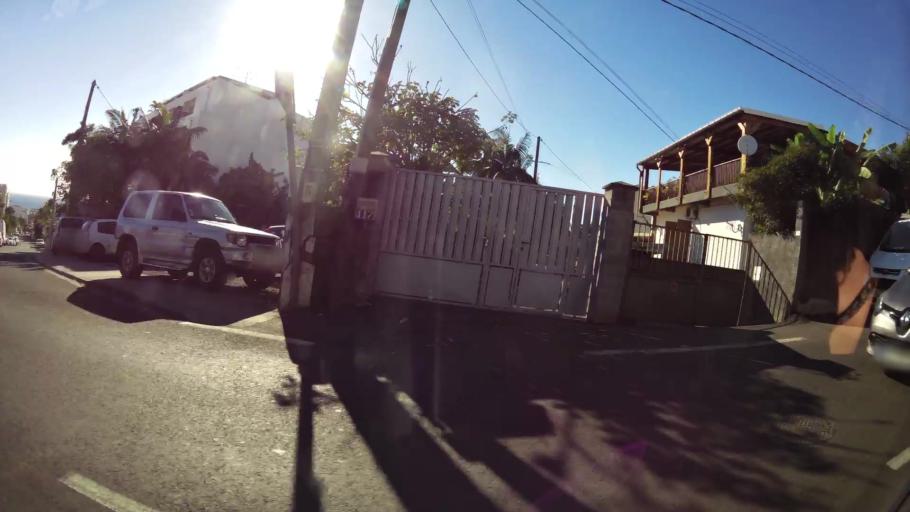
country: RE
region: Reunion
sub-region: Reunion
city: Saint-Denis
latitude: -20.9009
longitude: 55.4766
